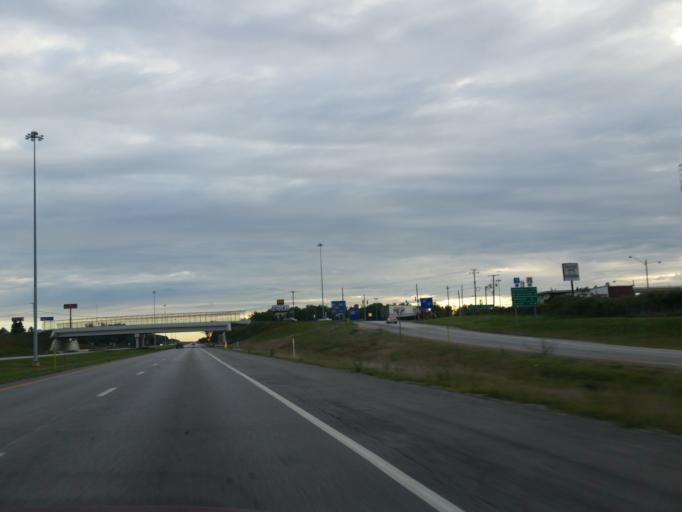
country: US
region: Ohio
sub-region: Ashtabula County
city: Geneva
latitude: 41.7854
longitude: -80.8574
